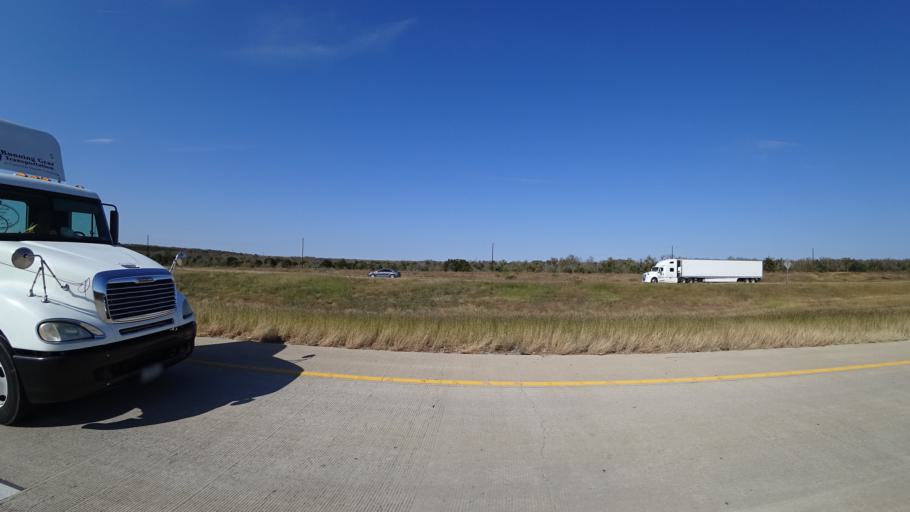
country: US
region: Texas
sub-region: Travis County
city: Hornsby Bend
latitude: 30.2775
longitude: -97.5858
